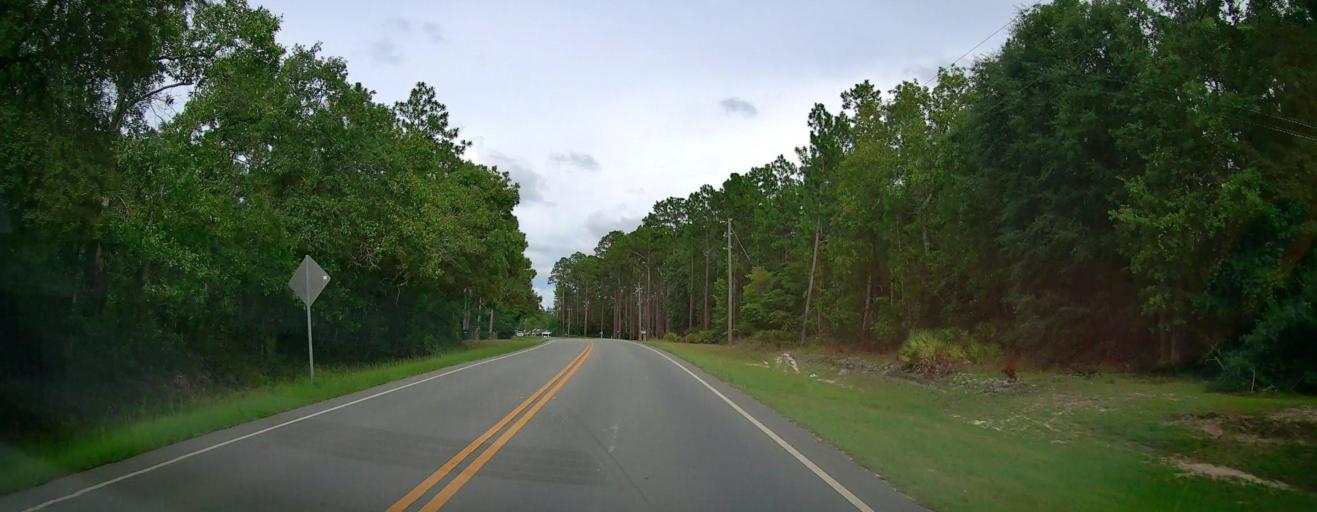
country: US
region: Georgia
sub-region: Wayne County
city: Jesup
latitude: 31.6572
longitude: -81.9074
